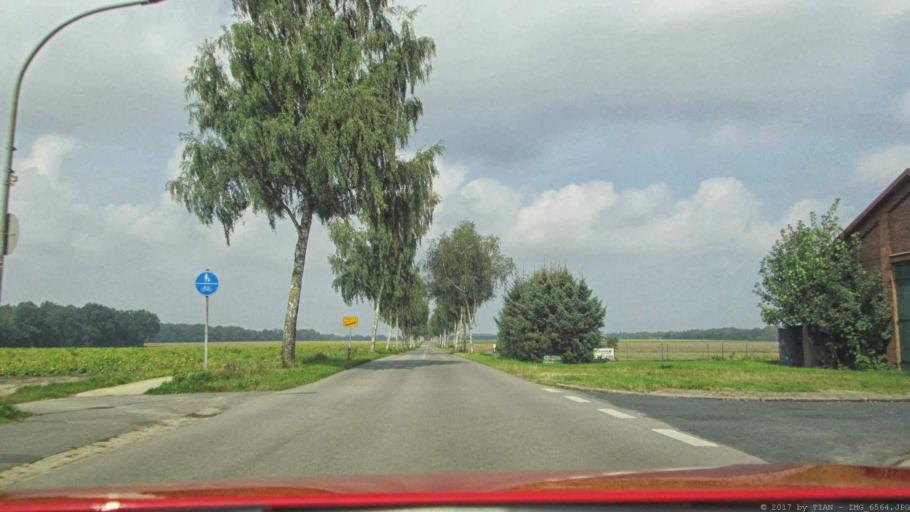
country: DE
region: Lower Saxony
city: Wrestedt
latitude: 52.9069
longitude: 10.5722
